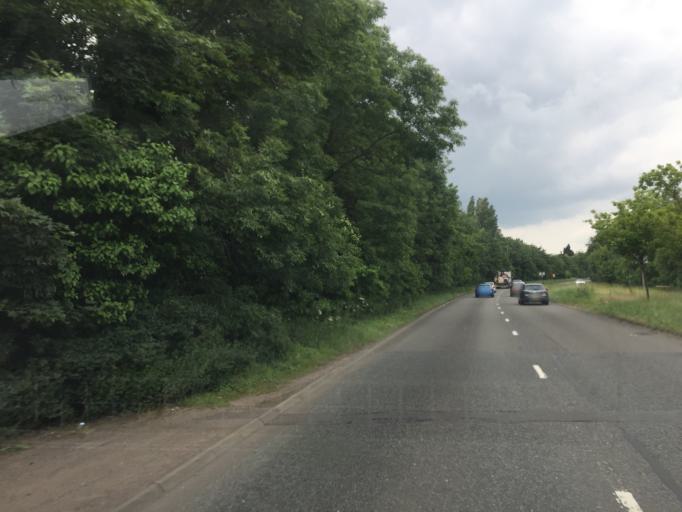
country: GB
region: England
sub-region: Sandwell
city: West Bromwich
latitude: 52.5137
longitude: -1.9788
